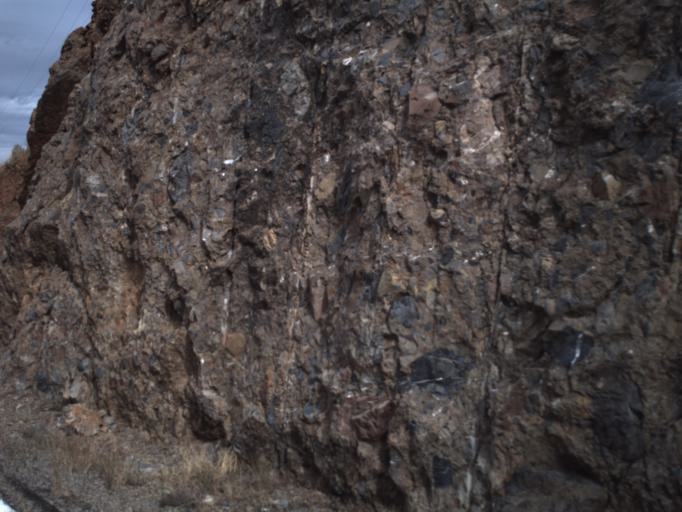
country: US
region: Utah
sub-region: Morgan County
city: Morgan
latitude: 40.9211
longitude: -111.6007
